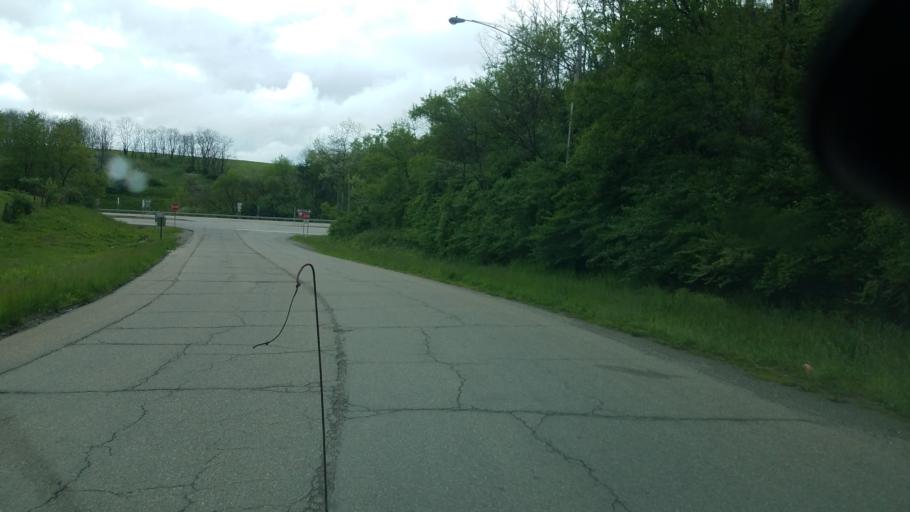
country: US
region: Ohio
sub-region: Harrison County
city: Cadiz
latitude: 40.2676
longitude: -81.0211
